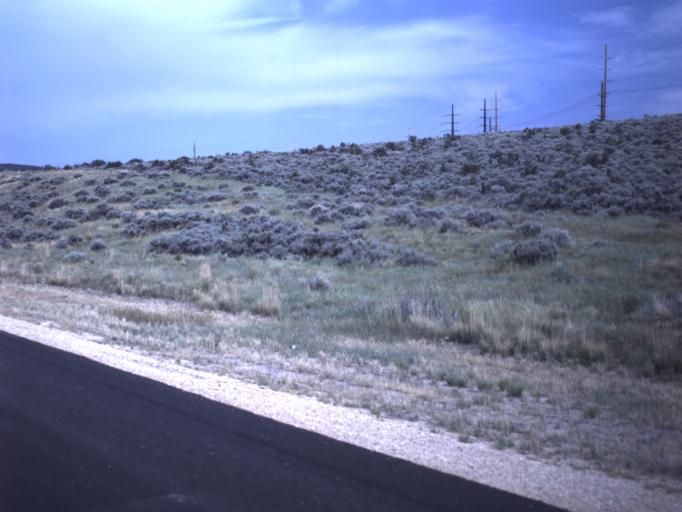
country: US
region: Utah
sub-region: Summit County
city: Park City
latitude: 40.6818
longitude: -111.4512
